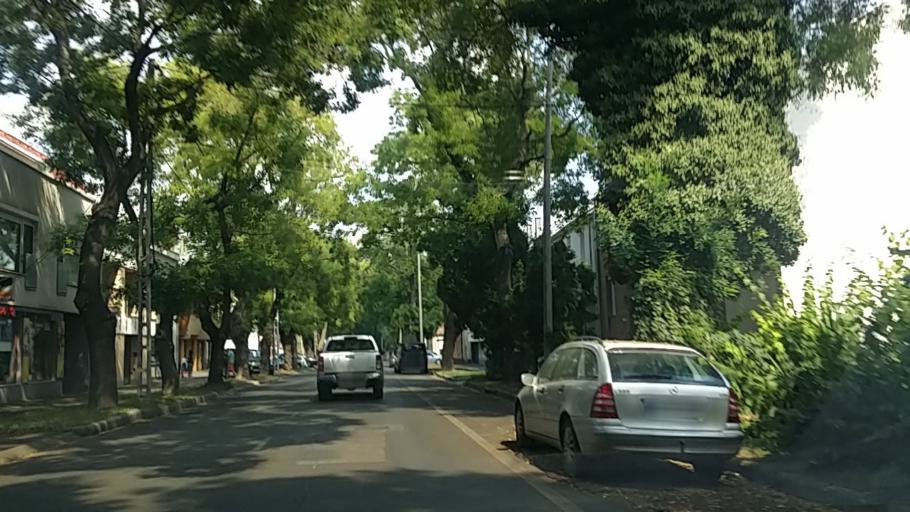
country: HU
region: Baranya
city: Pecs
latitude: 46.0713
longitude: 18.2021
